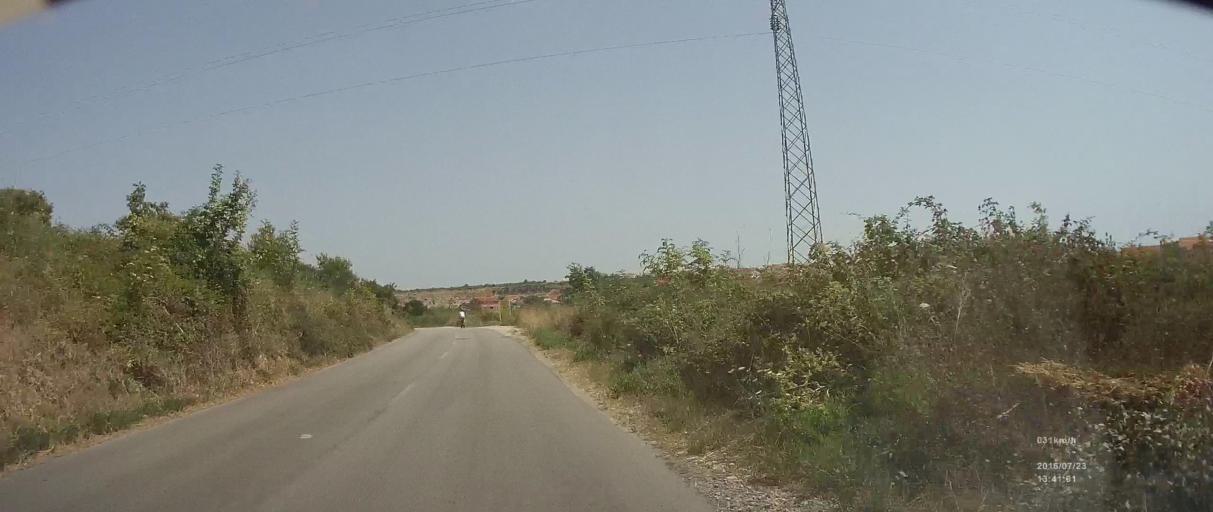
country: HR
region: Zadarska
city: Zadar
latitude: 44.1102
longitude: 15.2638
